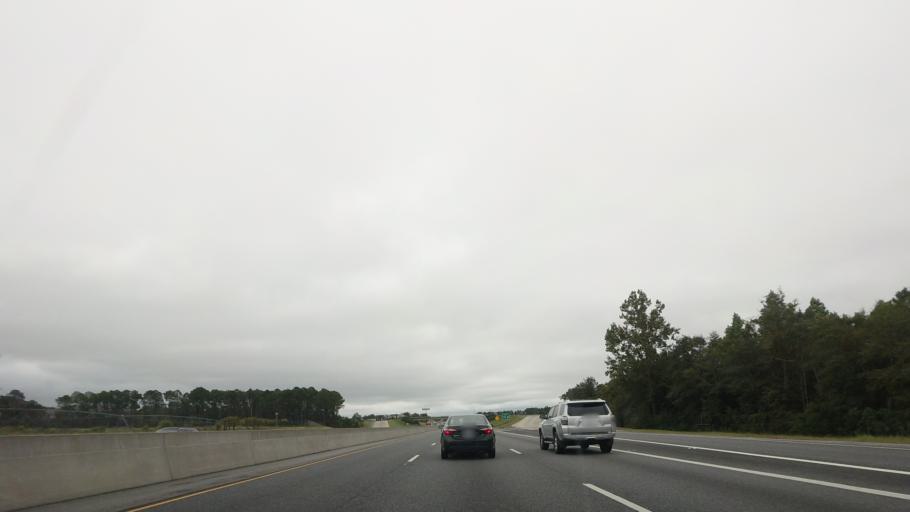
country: US
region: Georgia
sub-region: Turner County
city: Ashburn
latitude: 31.6686
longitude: -83.6101
